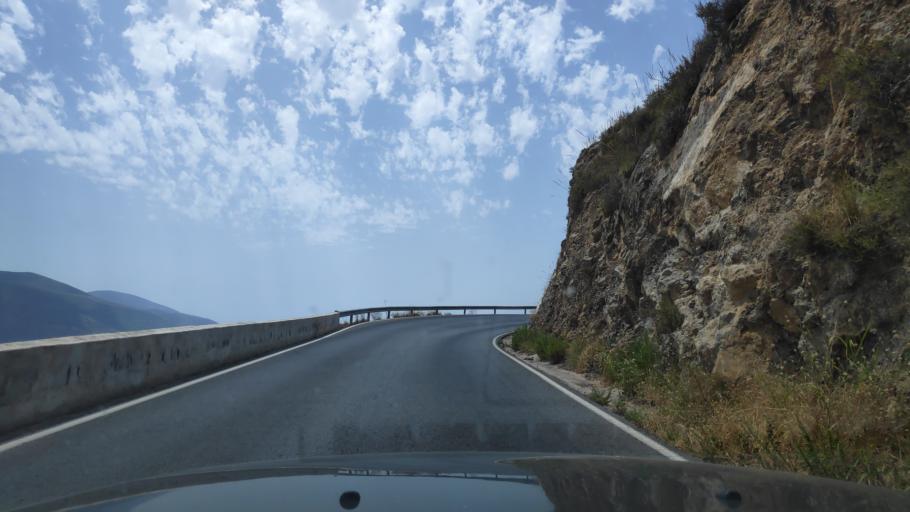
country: ES
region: Andalusia
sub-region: Provincia de Granada
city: Orjiva
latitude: 36.9121
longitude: -3.4291
